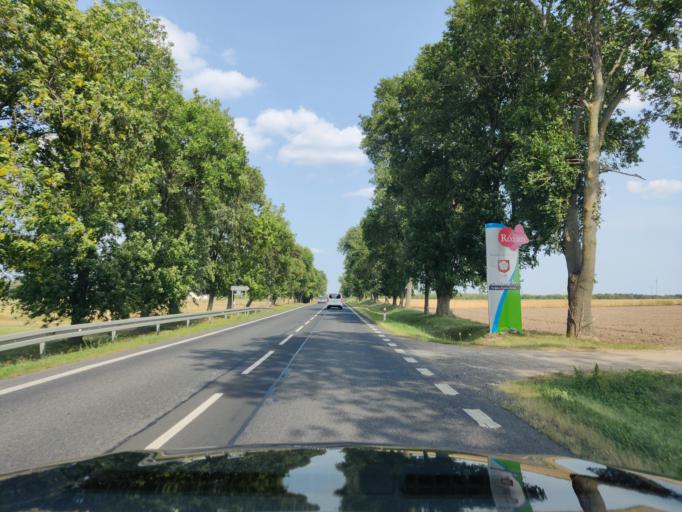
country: PL
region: Masovian Voivodeship
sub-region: Powiat makowski
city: Rozan
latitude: 52.8771
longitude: 21.3619
